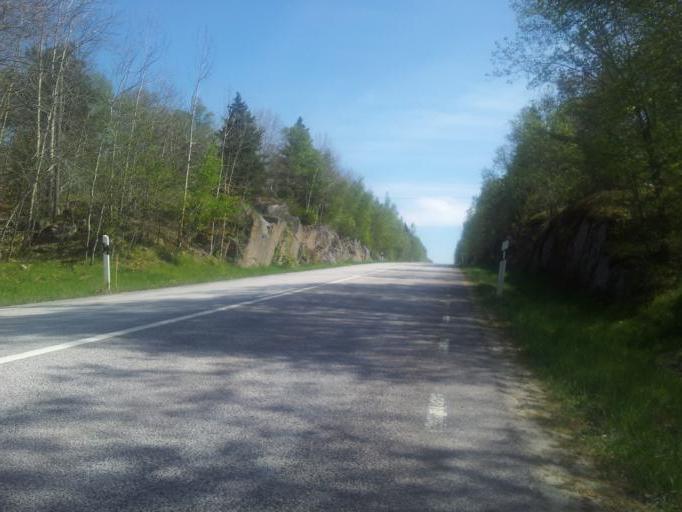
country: SE
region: Uppsala
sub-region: Knivsta Kommun
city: Knivsta
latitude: 59.8543
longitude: 17.8749
